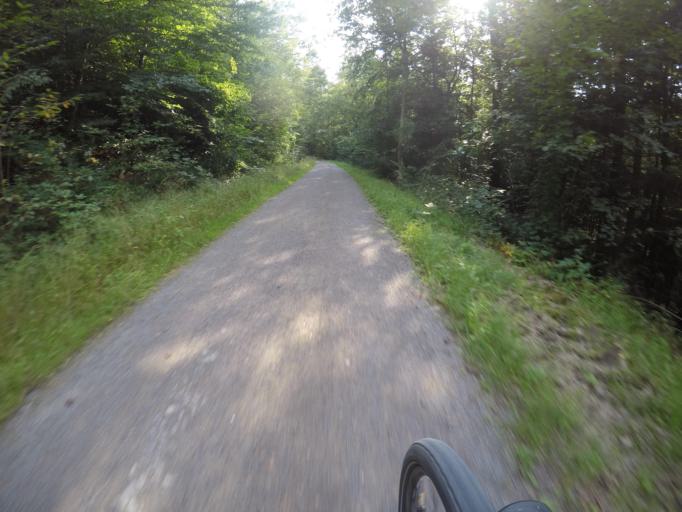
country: DE
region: Baden-Wuerttemberg
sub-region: Regierungsbezirk Stuttgart
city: Ostfildern
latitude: 48.7447
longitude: 9.2471
